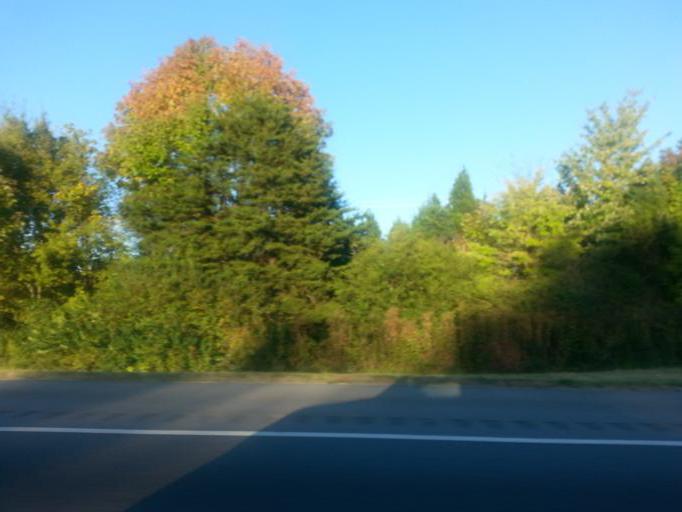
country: US
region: Tennessee
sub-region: Anderson County
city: Clinton
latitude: 36.0632
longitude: -84.0086
